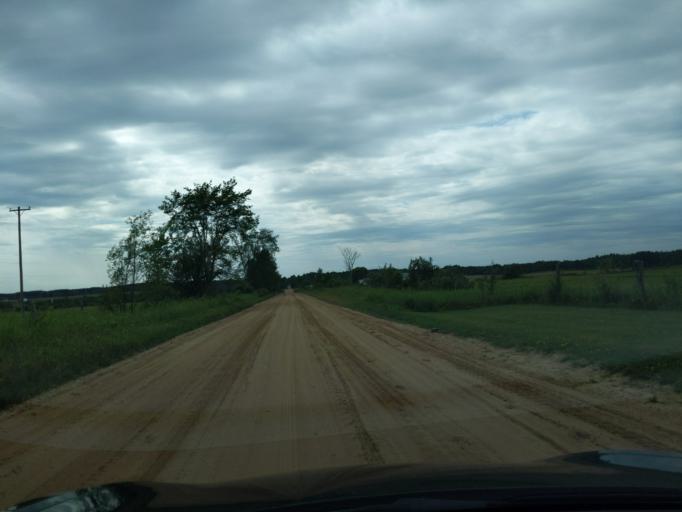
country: US
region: Michigan
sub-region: Clare County
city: Harrison
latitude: 44.0024
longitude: -84.9908
